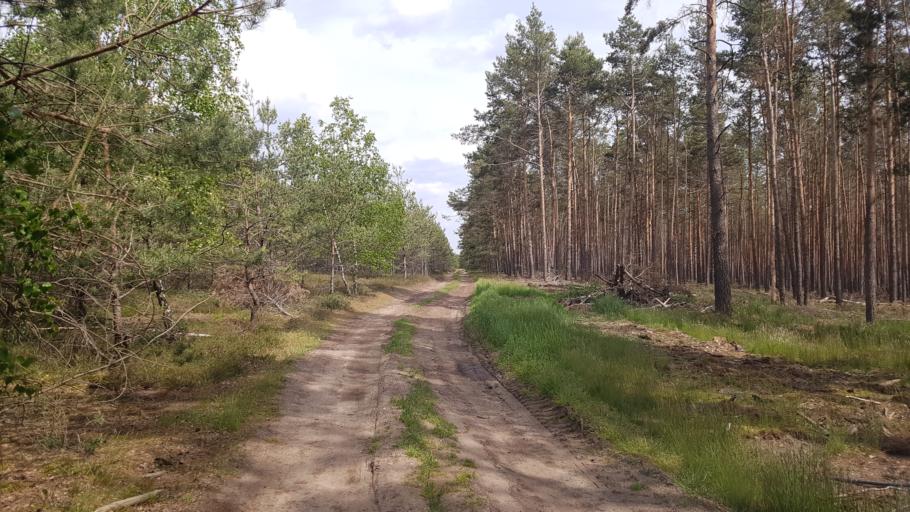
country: DE
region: Brandenburg
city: Doberlug-Kirchhain
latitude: 51.6147
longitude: 13.6272
